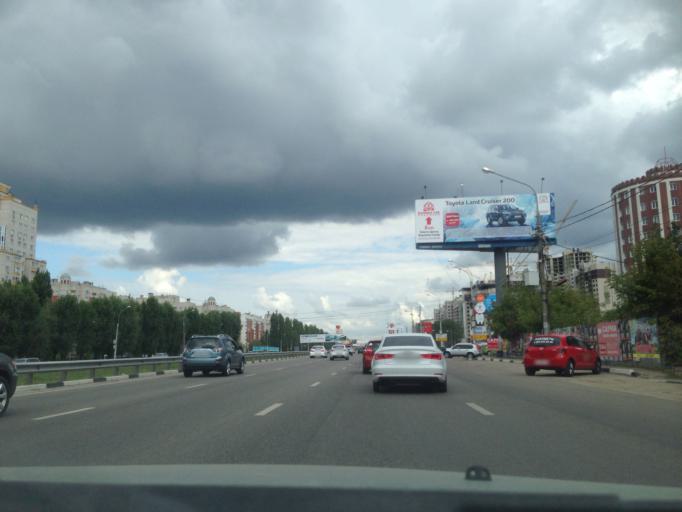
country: RU
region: Voronezj
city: Voronezh
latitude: 51.7103
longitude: 39.1811
